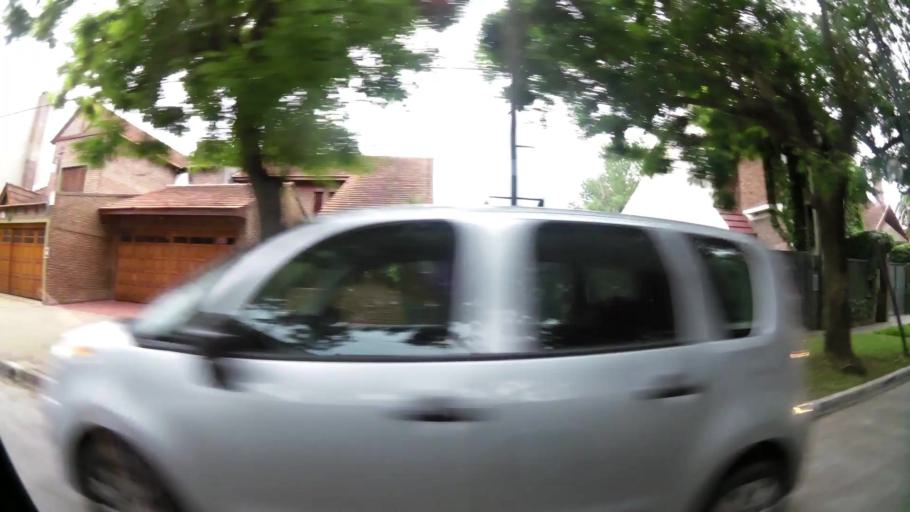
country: AR
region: Buenos Aires
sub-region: Partido de La Plata
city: La Plata
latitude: -34.9185
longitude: -57.9835
